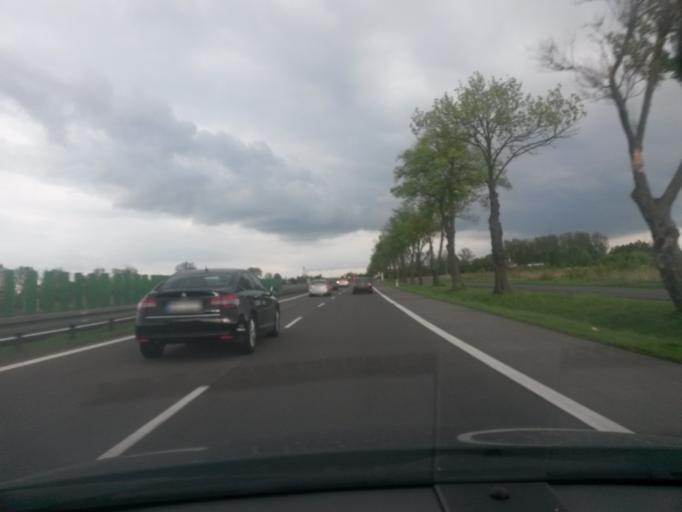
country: PL
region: Masovian Voivodeship
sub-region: Powiat plonski
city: Plonsk
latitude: 52.5916
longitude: 20.4456
